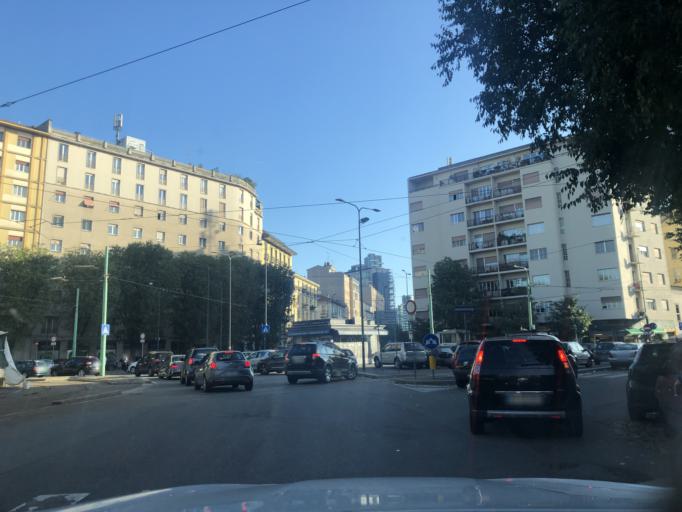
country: IT
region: Lombardy
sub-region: Citta metropolitana di Milano
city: Milano
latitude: 45.4895
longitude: 9.1907
